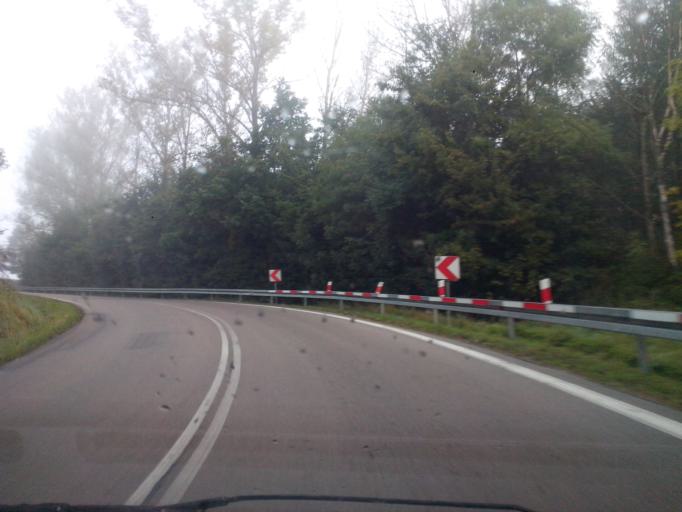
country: PL
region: Subcarpathian Voivodeship
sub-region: Powiat brzozowski
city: Domaradz
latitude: 49.7991
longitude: 21.9503
